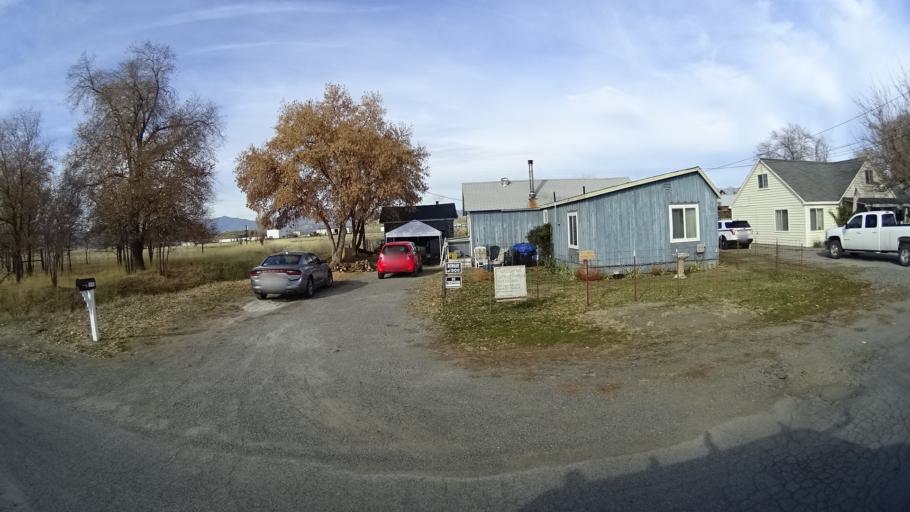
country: US
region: California
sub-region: Siskiyou County
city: Montague
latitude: 41.7225
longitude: -122.5278
